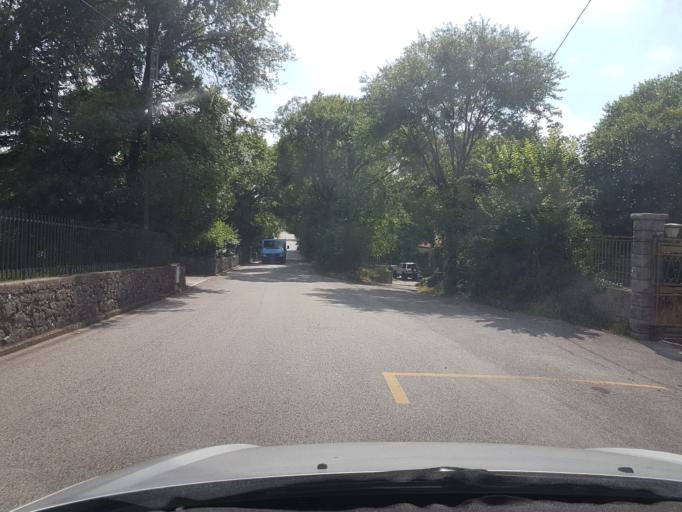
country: IT
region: Friuli Venezia Giulia
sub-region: Provincia di Trieste
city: Zolla
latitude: 45.7226
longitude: 13.7890
